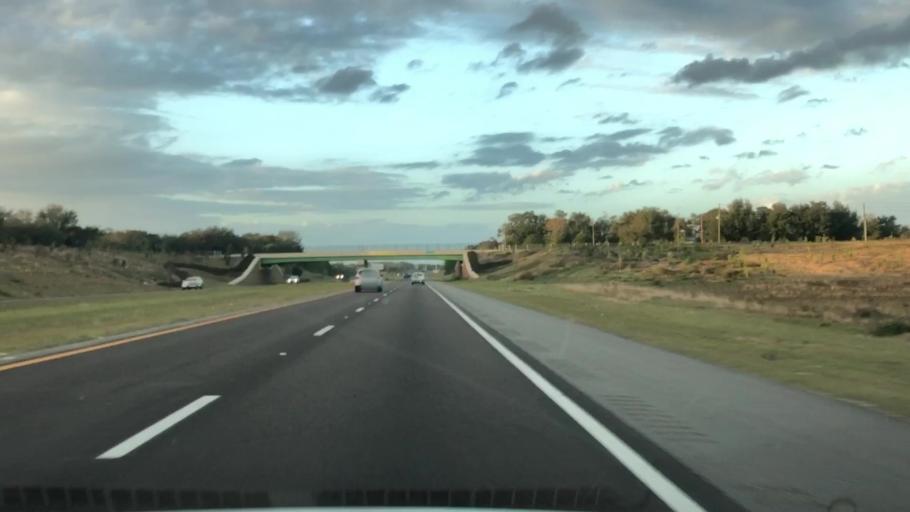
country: US
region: Florida
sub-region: Orange County
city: Zellwood
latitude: 28.7108
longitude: -81.5605
